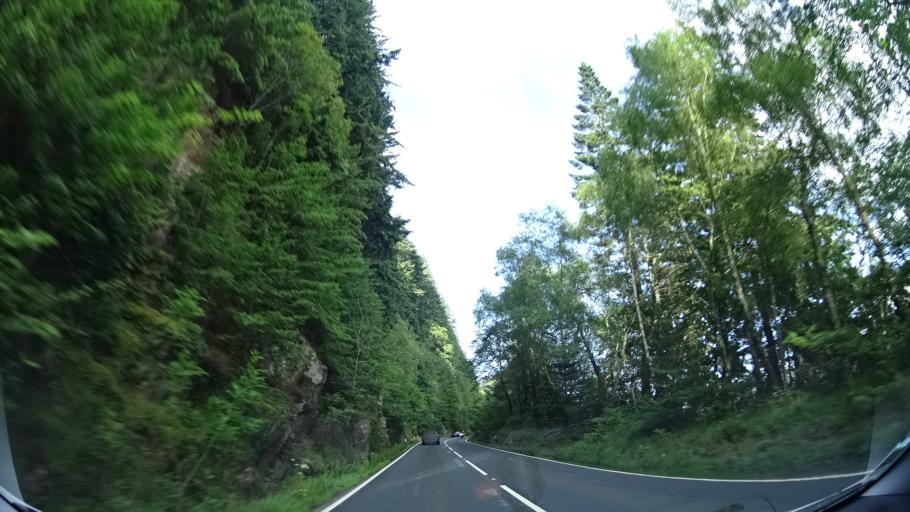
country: GB
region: Scotland
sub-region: Highland
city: Beauly
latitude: 57.2733
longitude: -4.5011
